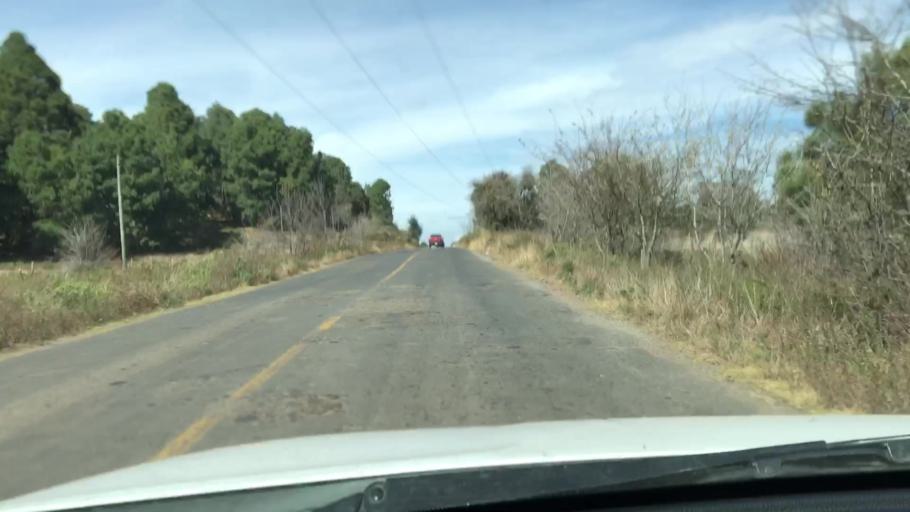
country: MX
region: Jalisco
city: Chiquilistlan
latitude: 20.1052
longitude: -103.7182
